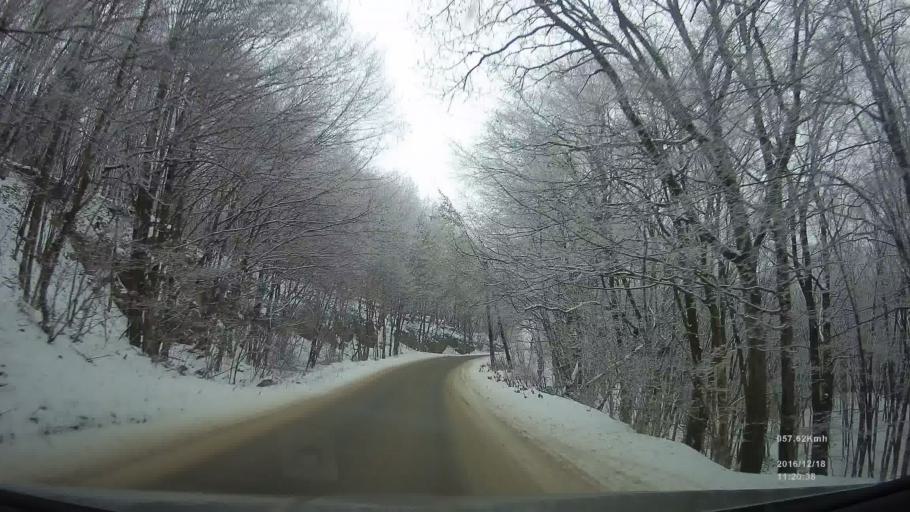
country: SK
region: Presovsky
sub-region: Okres Presov
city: Presov
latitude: 48.9089
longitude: 21.3618
